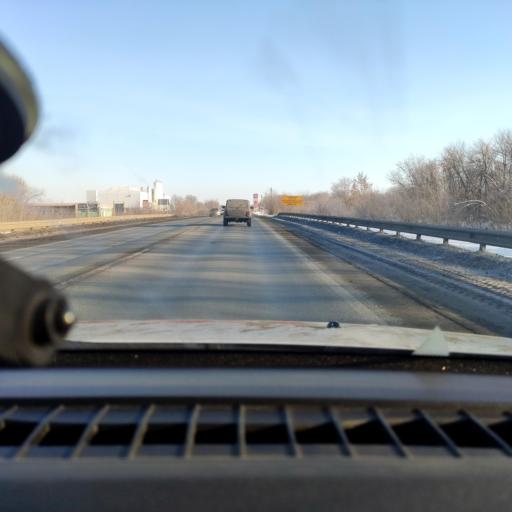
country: RU
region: Samara
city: Samara
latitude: 53.0812
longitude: 50.1094
